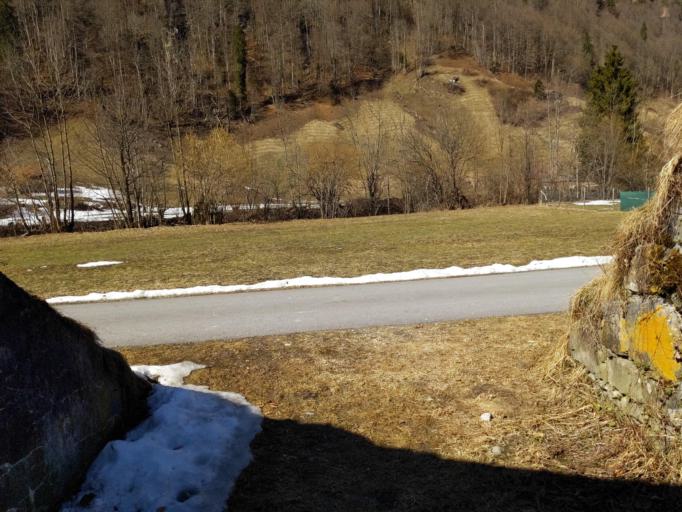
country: CH
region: Glarus
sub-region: Glarus
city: Luchsingen
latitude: 46.9502
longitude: 9.0272
